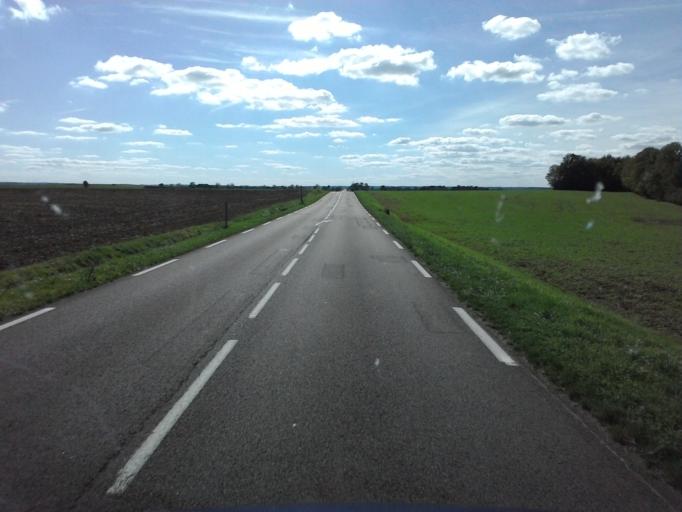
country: FR
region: Bourgogne
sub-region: Departement de la Cote-d'Or
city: Chatillon-sur-Seine
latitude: 47.8924
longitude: 4.6066
